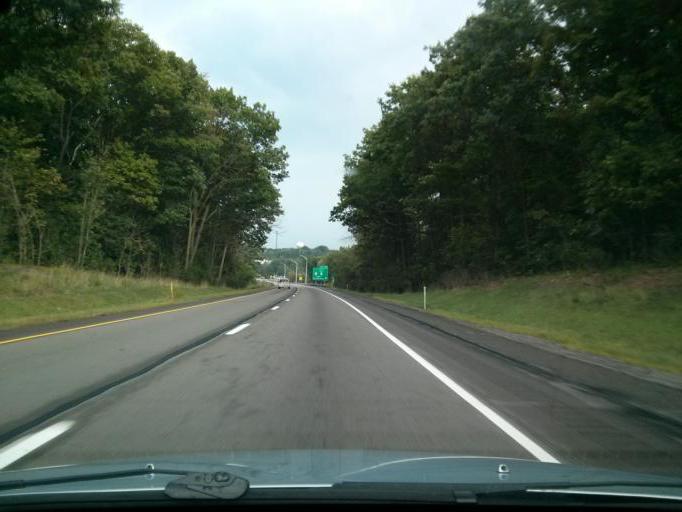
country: US
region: Pennsylvania
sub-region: Jefferson County
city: Brookville
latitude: 41.1717
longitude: -79.1067
